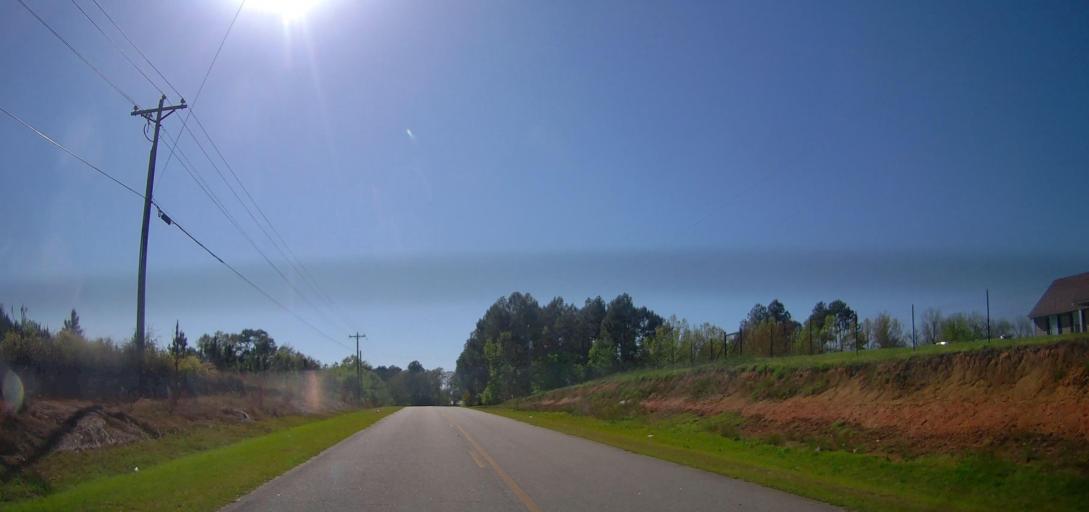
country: US
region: Georgia
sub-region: Pulaski County
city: Hawkinsville
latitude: 32.2479
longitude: -83.4935
